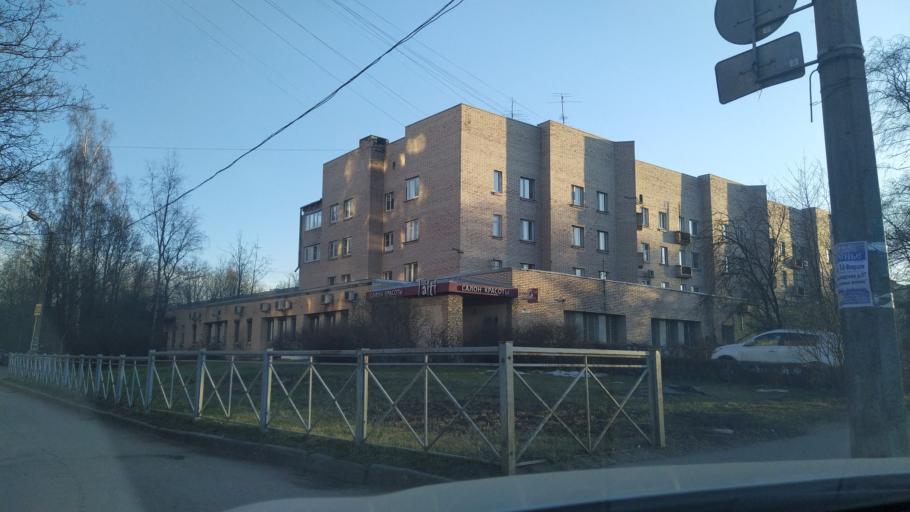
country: RU
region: St.-Petersburg
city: Pushkin
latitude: 59.7301
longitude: 30.4056
